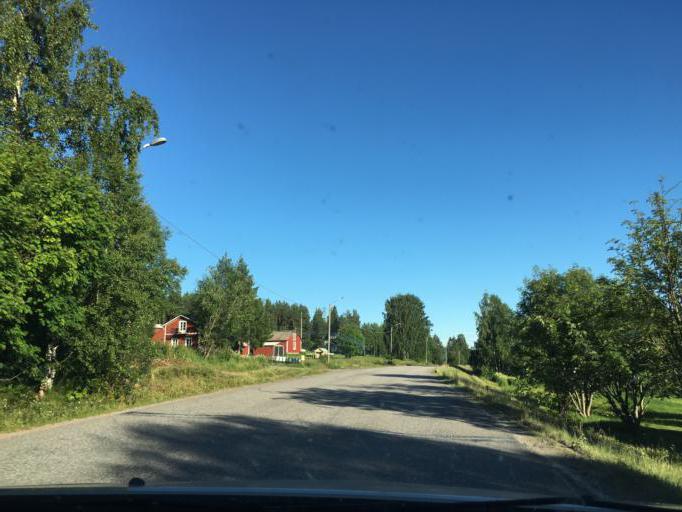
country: SE
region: Norrbotten
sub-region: Kalix Kommun
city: Rolfs
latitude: 65.9227
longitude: 22.9108
